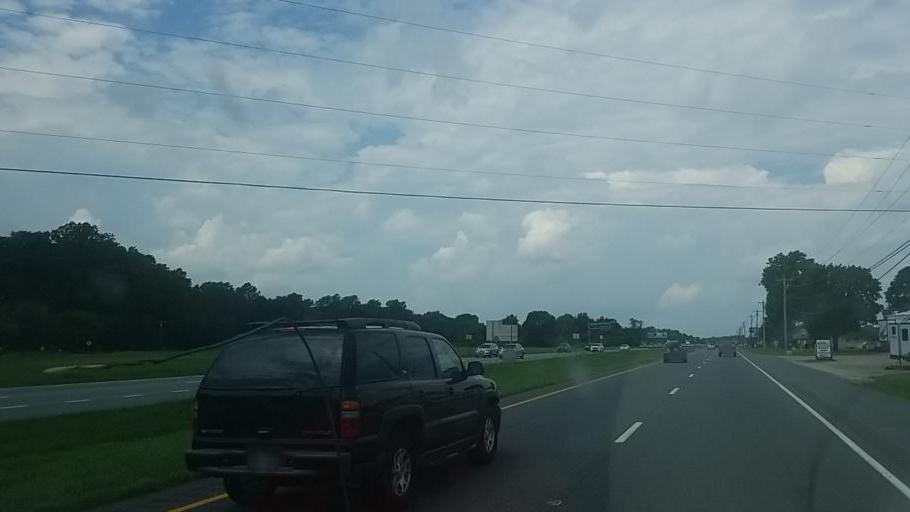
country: US
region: Delaware
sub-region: Sussex County
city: Milford
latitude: 38.9692
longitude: -75.4334
